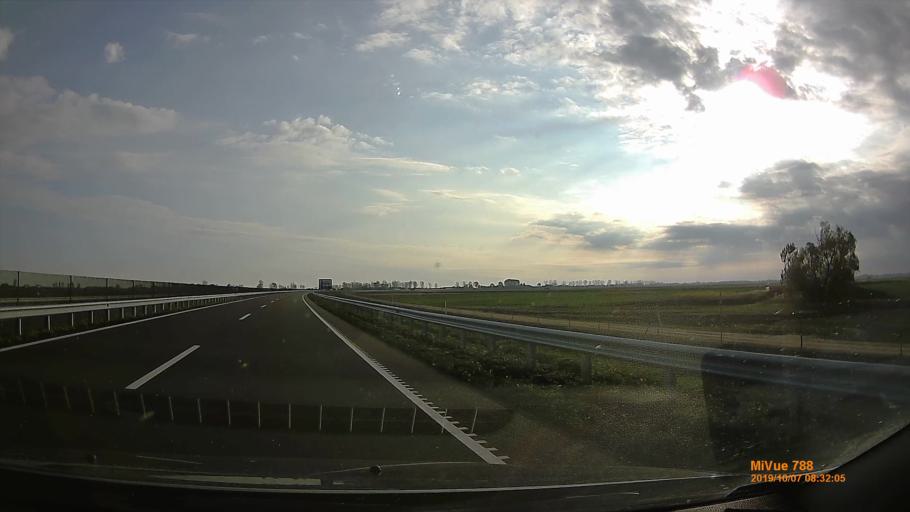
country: HU
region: Bekes
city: Bekesszentandras
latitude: 46.8251
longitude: 20.4597
